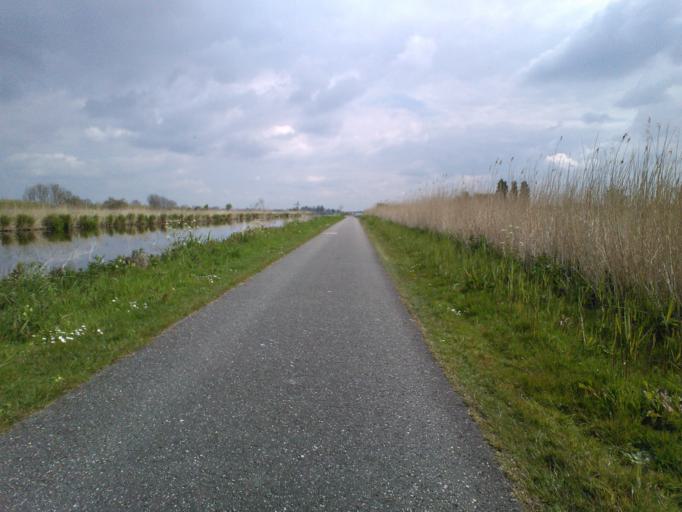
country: NL
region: South Holland
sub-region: Gemeente Maassluis
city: Maassluis
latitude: 51.9365
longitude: 4.2964
